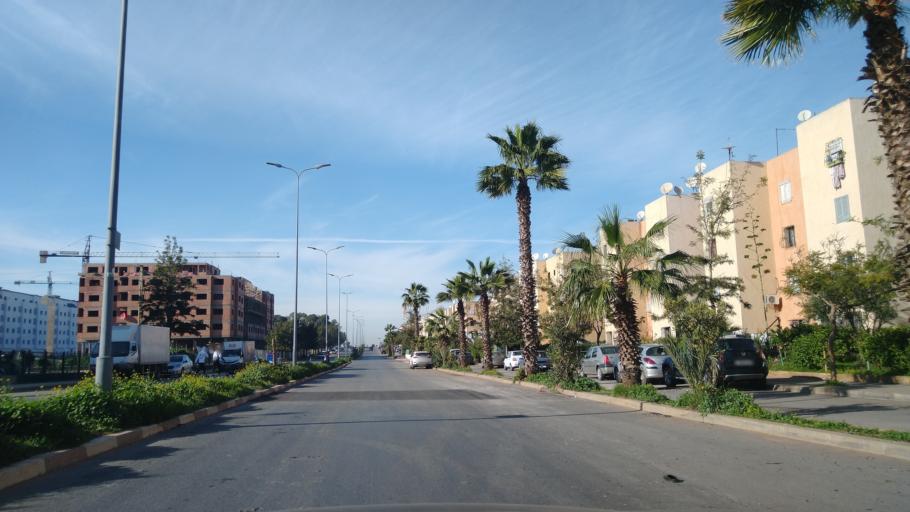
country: MA
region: Rabat-Sale-Zemmour-Zaer
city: Sale
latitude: 33.9944
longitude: -6.7450
